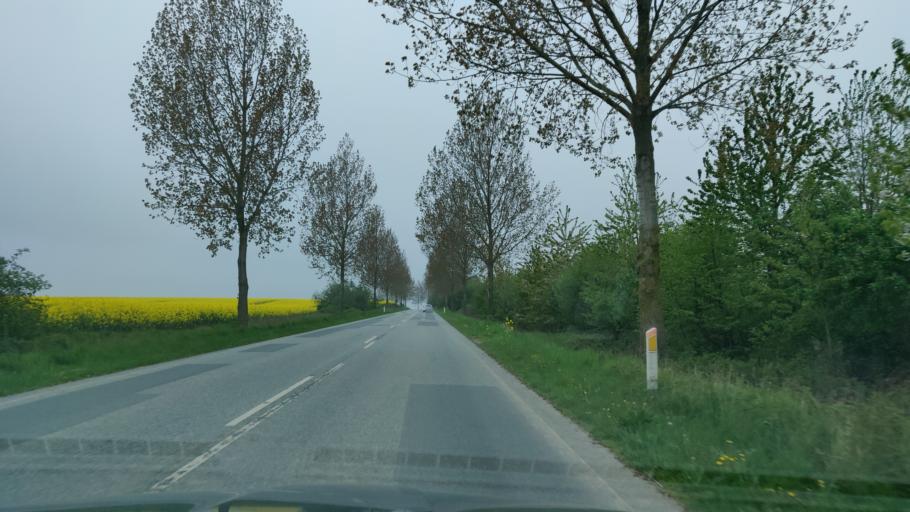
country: DK
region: South Denmark
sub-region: Sonderborg Kommune
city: Guderup
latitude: 54.9863
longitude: 9.8791
